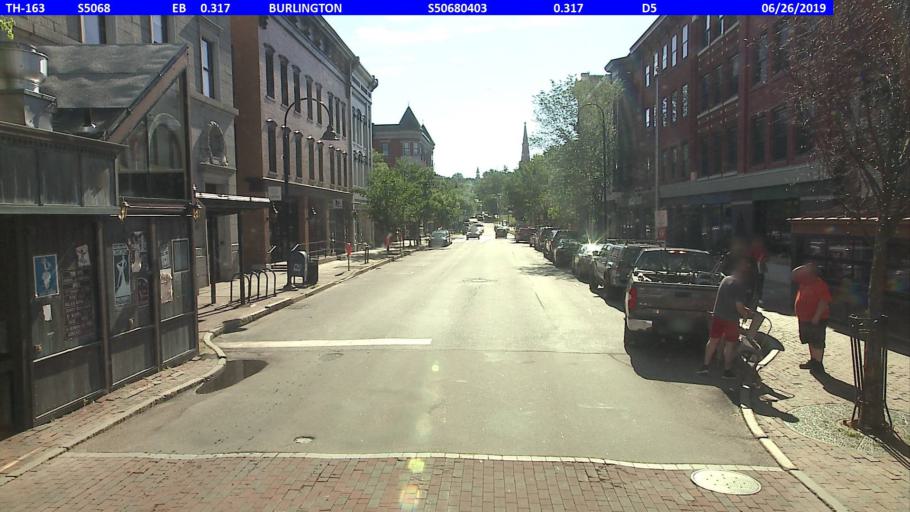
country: US
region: Vermont
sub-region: Chittenden County
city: Burlington
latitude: 44.4771
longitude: -73.2125
